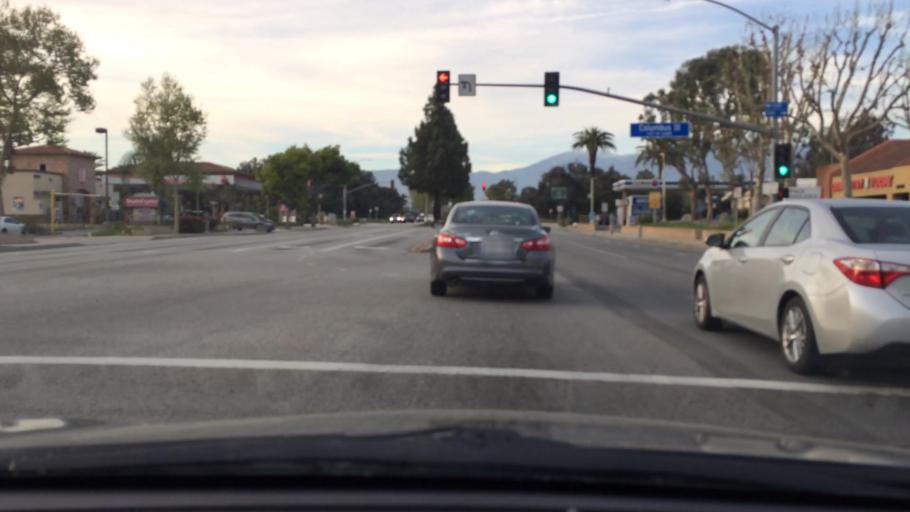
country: US
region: California
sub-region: San Bernardino County
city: Chino
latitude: 34.0280
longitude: -117.6894
